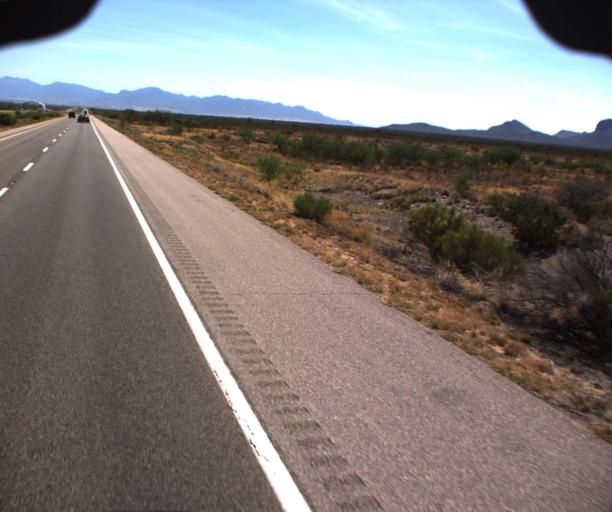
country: US
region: Arizona
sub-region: Cochise County
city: Huachuca City
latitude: 31.7566
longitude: -110.3503
